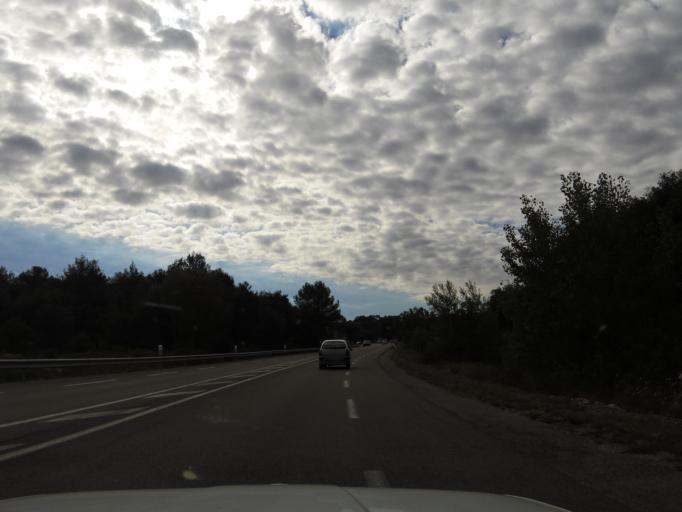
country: FR
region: Languedoc-Roussillon
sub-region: Departement du Gard
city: La Calmette
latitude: 43.8885
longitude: 4.2953
